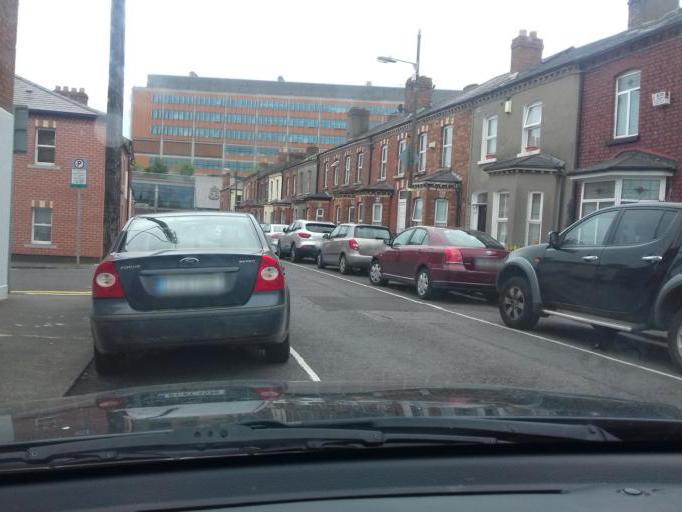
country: IE
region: Leinster
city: Drumcondra
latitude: 53.3612
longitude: -6.2649
